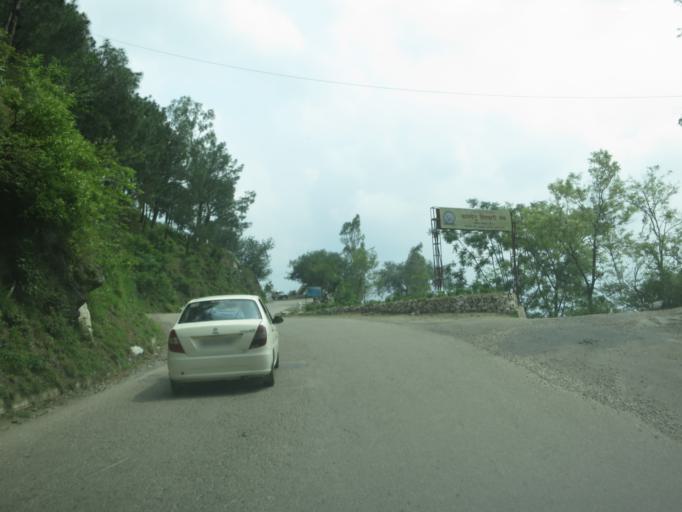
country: IN
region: Himachal Pradesh
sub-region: Bilaspur
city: Bilaspur
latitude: 31.2593
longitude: 76.8692
